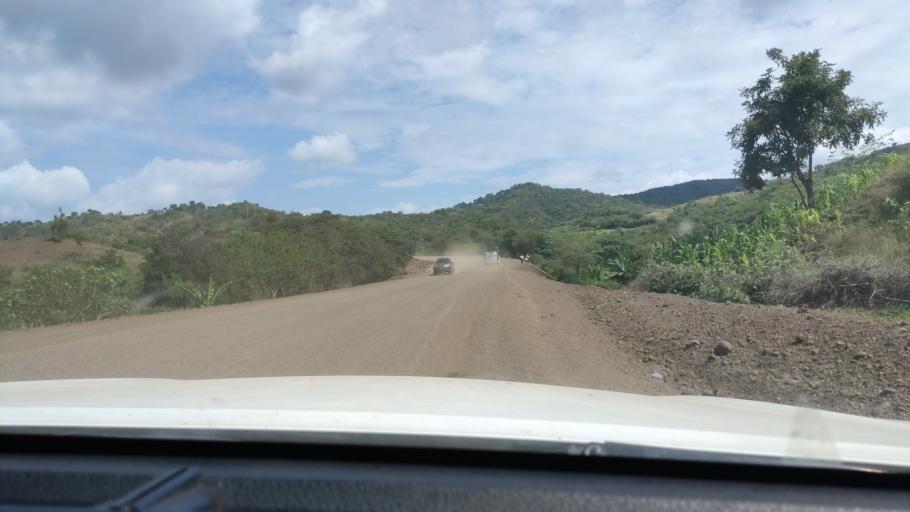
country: ET
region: Southern Nations, Nationalities, and People's Region
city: Felege Neway
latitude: 6.3911
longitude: 37.0612
